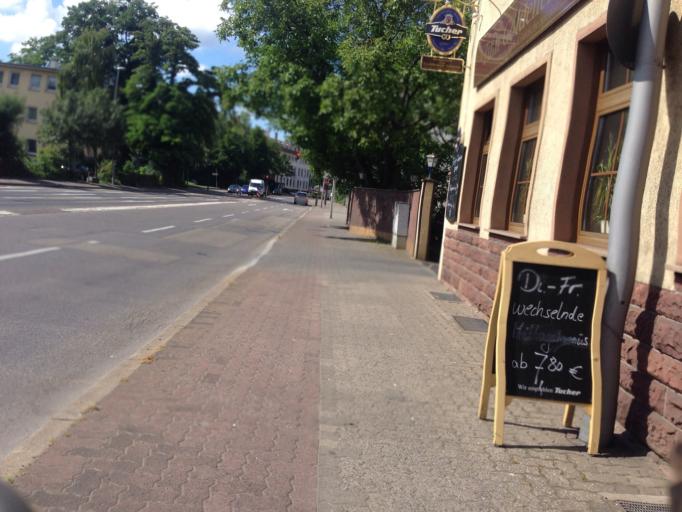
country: DE
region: Hesse
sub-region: Regierungsbezirk Darmstadt
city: Hanau am Main
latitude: 50.1371
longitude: 8.9123
